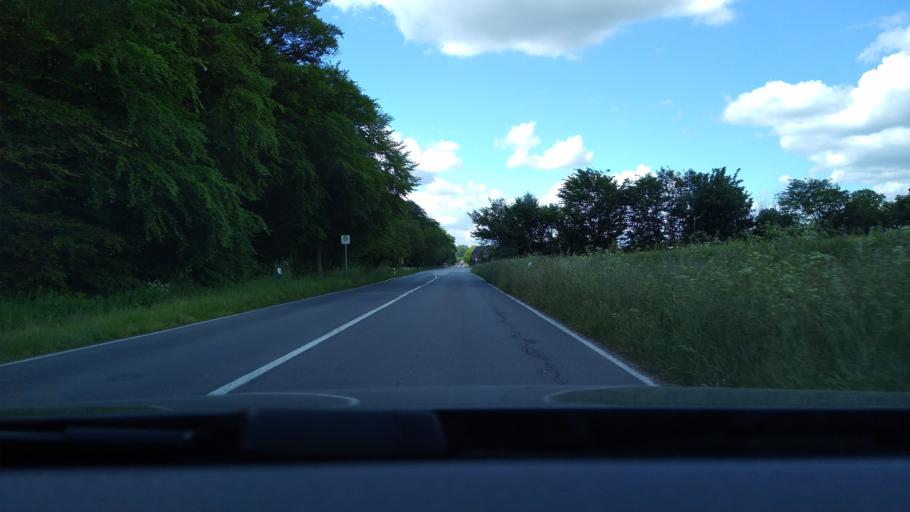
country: DE
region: Schleswig-Holstein
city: Kellenhusen
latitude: 54.2079
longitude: 11.0419
